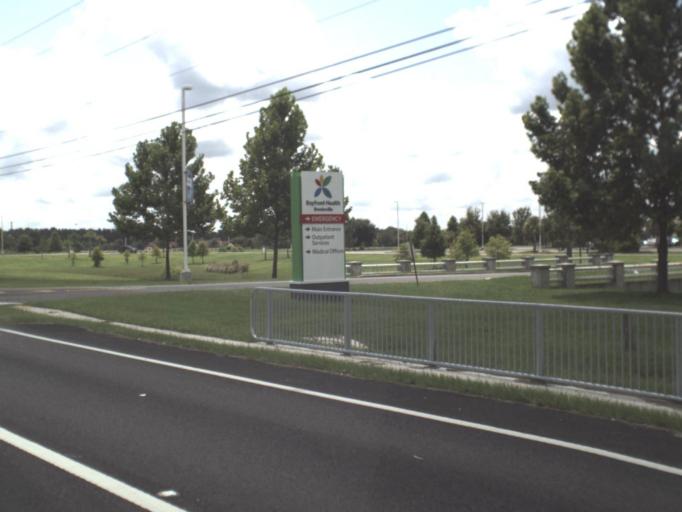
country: US
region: Florida
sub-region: Hernando County
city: South Brooksville
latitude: 28.5411
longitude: -82.4438
